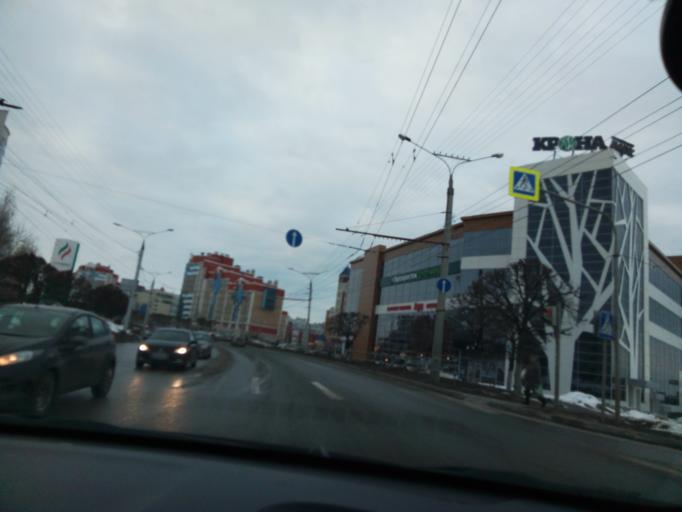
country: RU
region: Chuvashia
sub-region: Cheboksarskiy Rayon
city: Cheboksary
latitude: 56.1482
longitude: 47.2013
